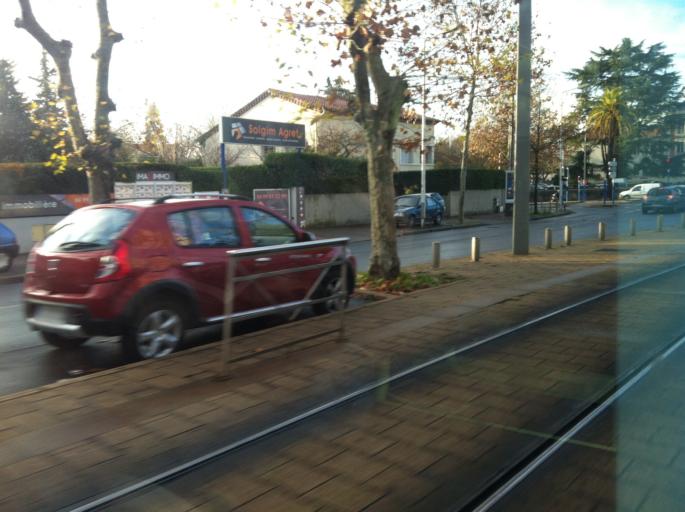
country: FR
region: Languedoc-Roussillon
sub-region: Departement de l'Herault
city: Montpellier
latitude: 43.6281
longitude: 3.8591
